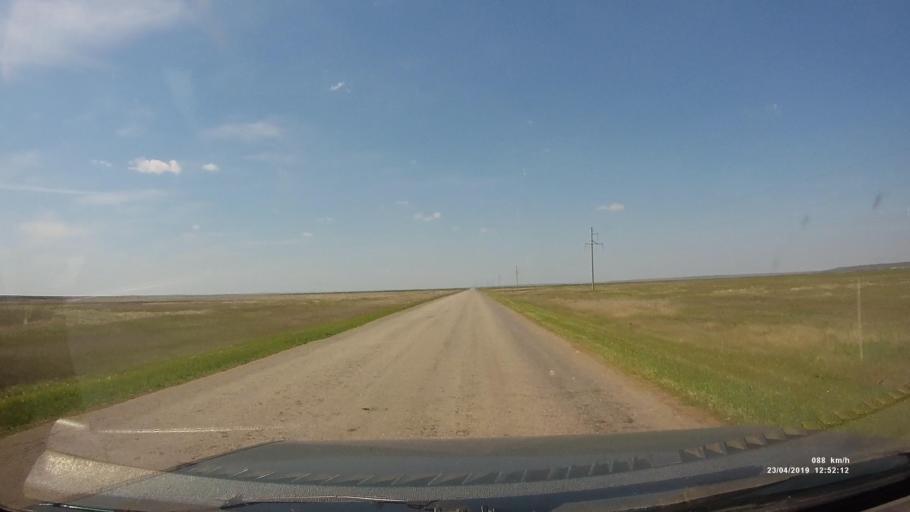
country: RU
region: Kalmykiya
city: Yashalta
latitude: 46.5622
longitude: 42.6128
